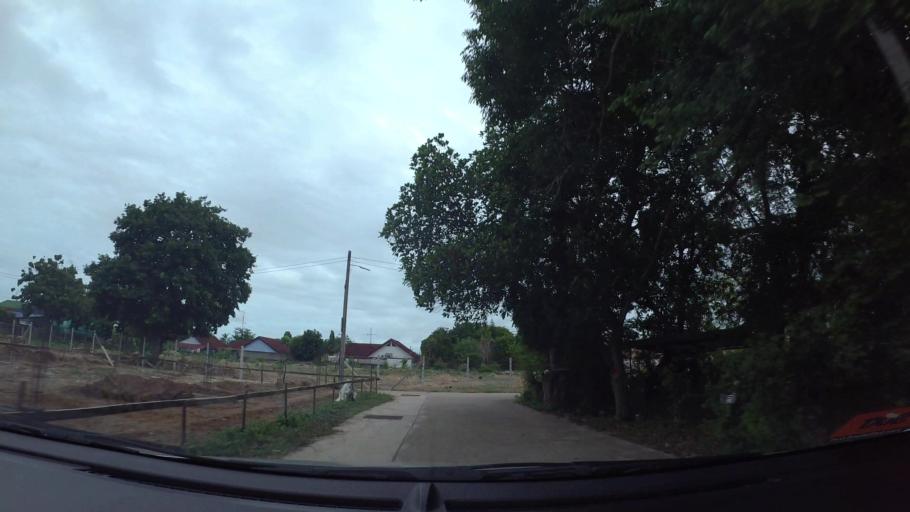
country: TH
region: Chon Buri
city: Sattahip
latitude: 12.6865
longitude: 100.9007
